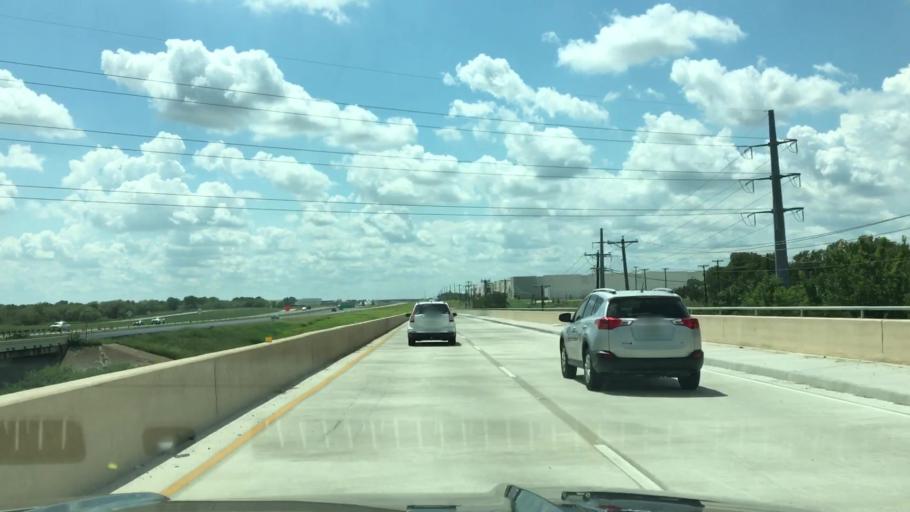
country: US
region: Texas
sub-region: Denton County
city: Roanoke
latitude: 33.0159
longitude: -97.2828
